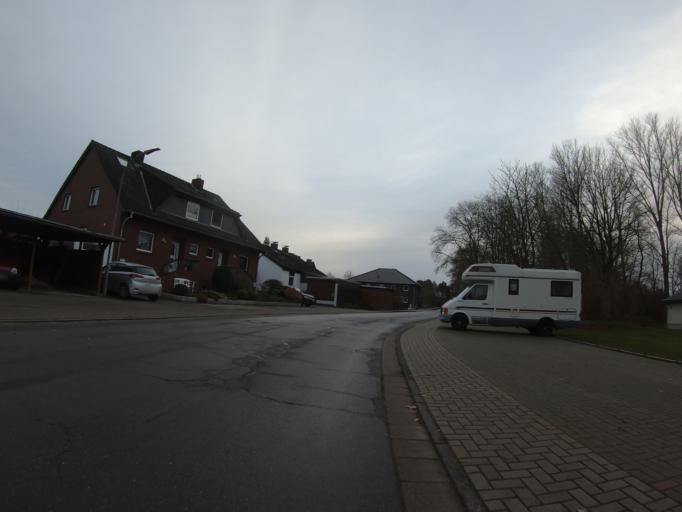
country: DE
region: Lower Saxony
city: Isenbuttel
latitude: 52.4277
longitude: 10.5804
